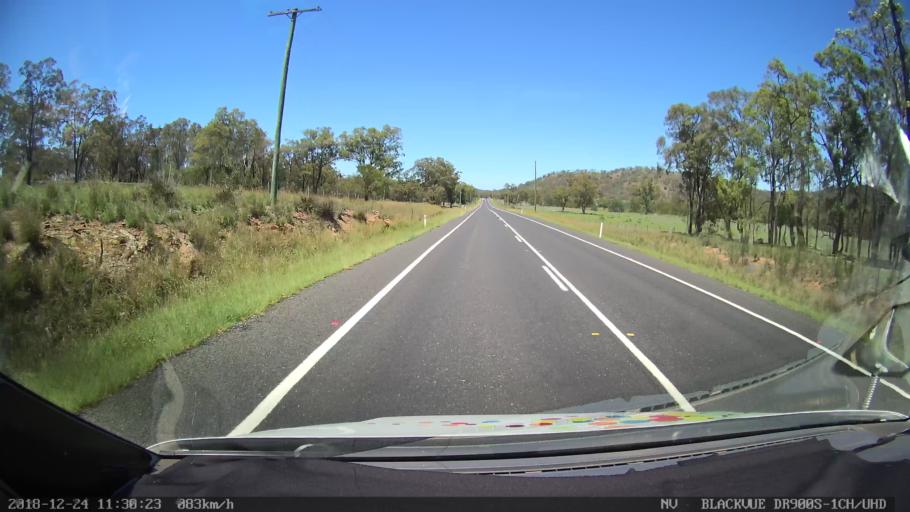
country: AU
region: New South Wales
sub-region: Upper Hunter Shire
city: Merriwa
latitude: -32.2040
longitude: 150.4669
